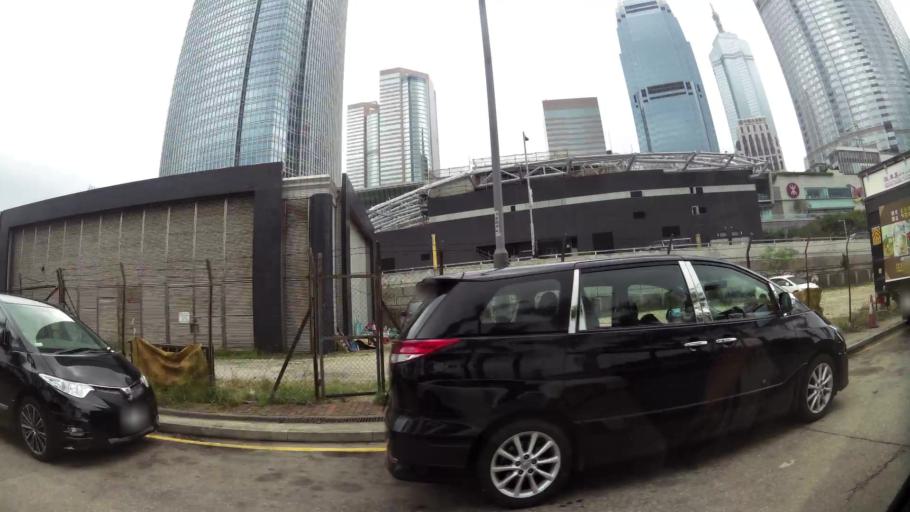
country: HK
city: Hong Kong
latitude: 22.2867
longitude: 114.1592
